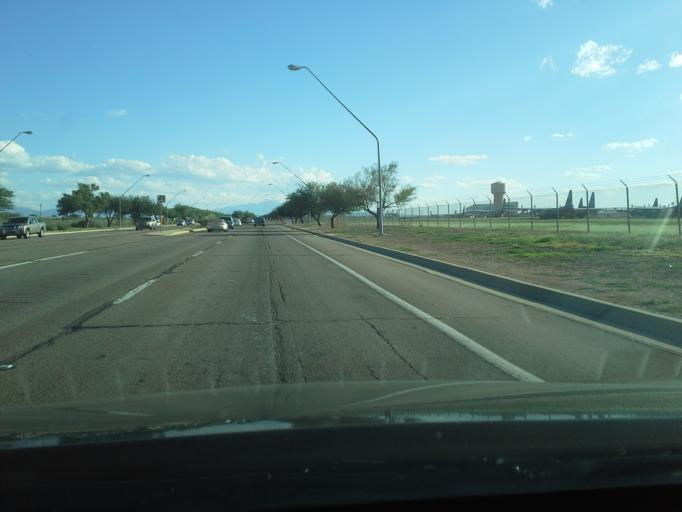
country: US
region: Arizona
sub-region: Pima County
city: Tucson
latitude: 32.1691
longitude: -110.8410
